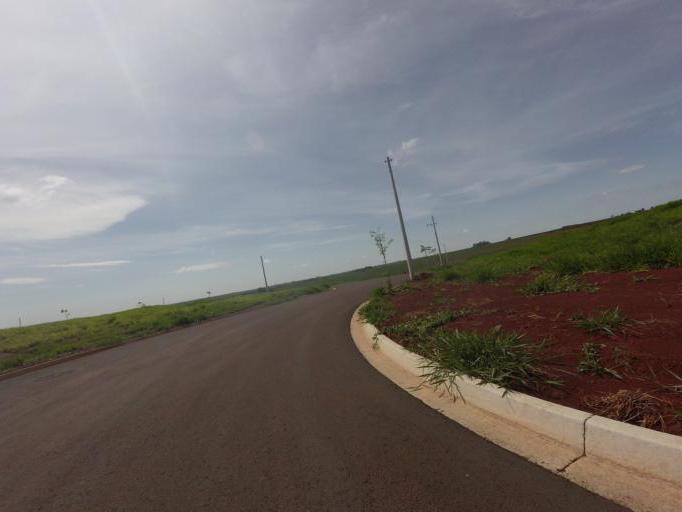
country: BR
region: Sao Paulo
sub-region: Piracicaba
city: Piracicaba
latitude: -22.7610
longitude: -47.5806
